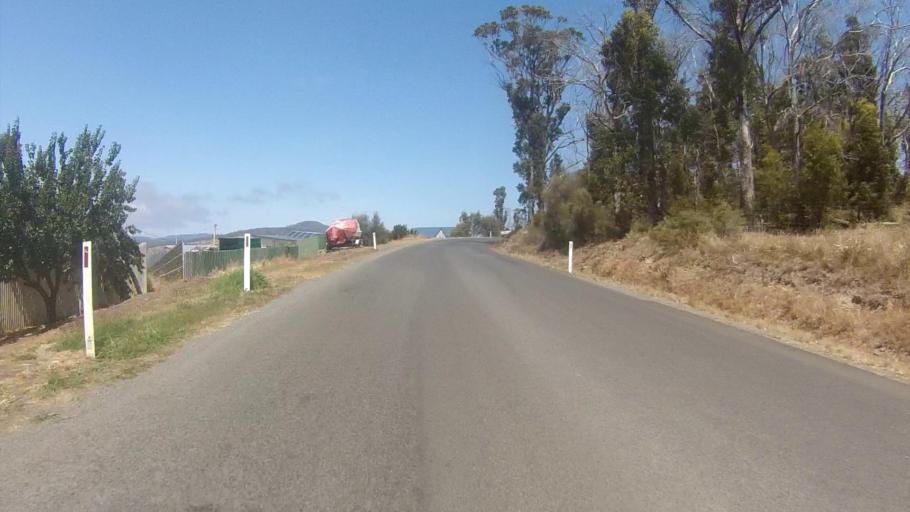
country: AU
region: Tasmania
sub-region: Sorell
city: Sorell
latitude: -42.8717
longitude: 147.8265
